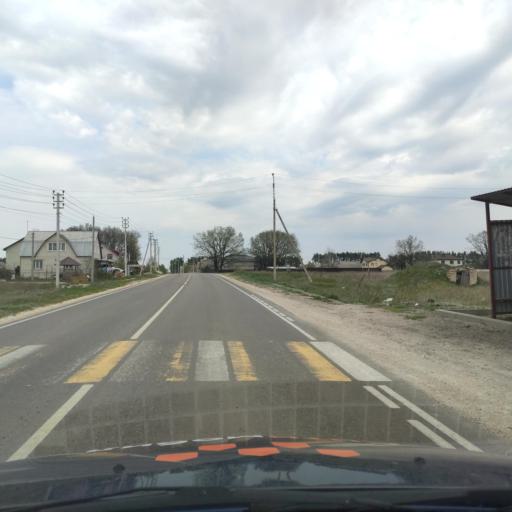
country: RU
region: Voronezj
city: Podgornoye
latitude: 51.8717
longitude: 39.1729
